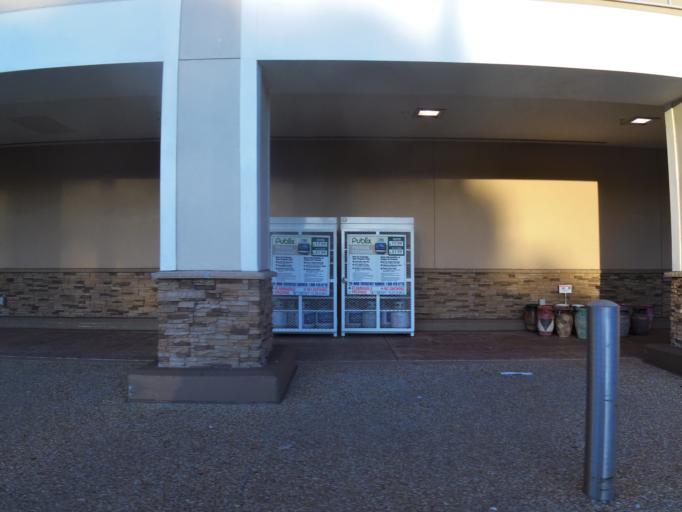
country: US
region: Florida
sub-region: Duval County
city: Atlantic Beach
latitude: 30.3620
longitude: -81.5017
